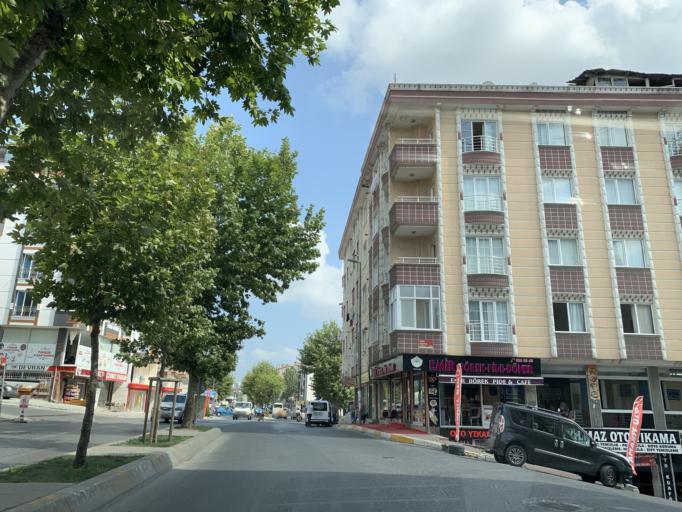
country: TR
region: Istanbul
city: Esenyurt
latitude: 41.0401
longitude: 28.6617
